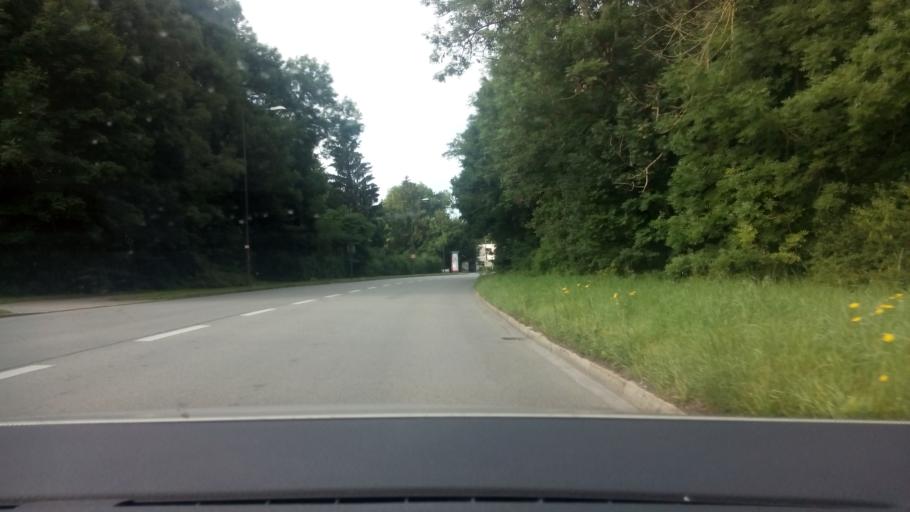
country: DE
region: Bavaria
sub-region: Upper Bavaria
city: Unterfoehring
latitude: 48.1932
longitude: 11.6227
